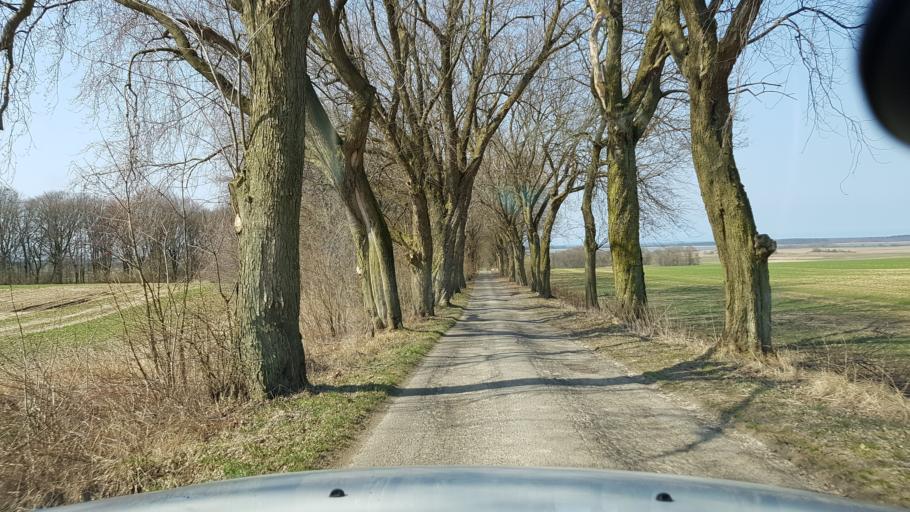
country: PL
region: West Pomeranian Voivodeship
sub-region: Powiat slawienski
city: Darlowo
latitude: 54.4658
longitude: 16.4984
